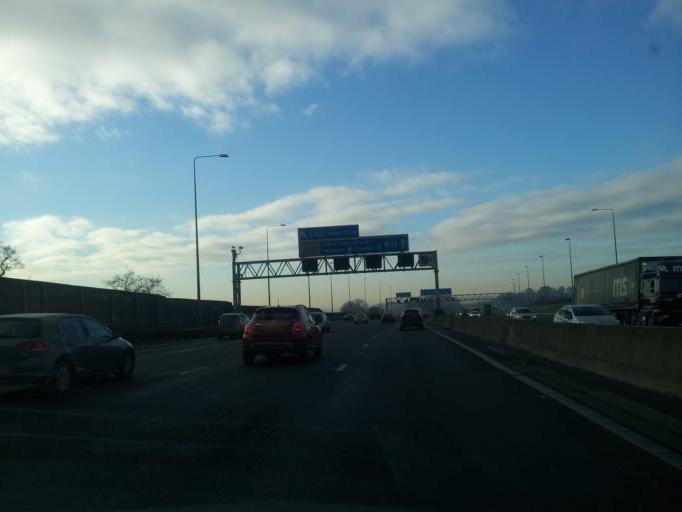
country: GB
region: England
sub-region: Hertfordshire
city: Chorleywood
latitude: 51.6422
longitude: -0.5029
